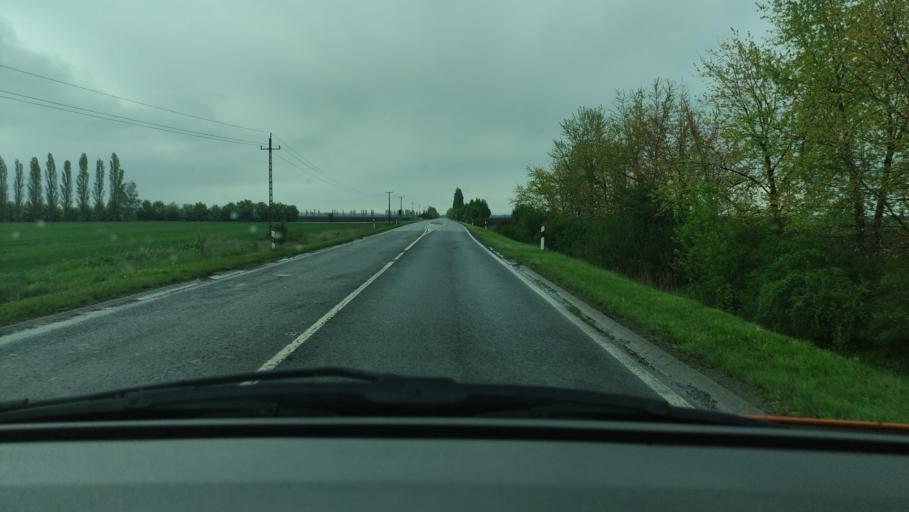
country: HU
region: Baranya
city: Mohacs
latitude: 45.9875
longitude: 18.6576
